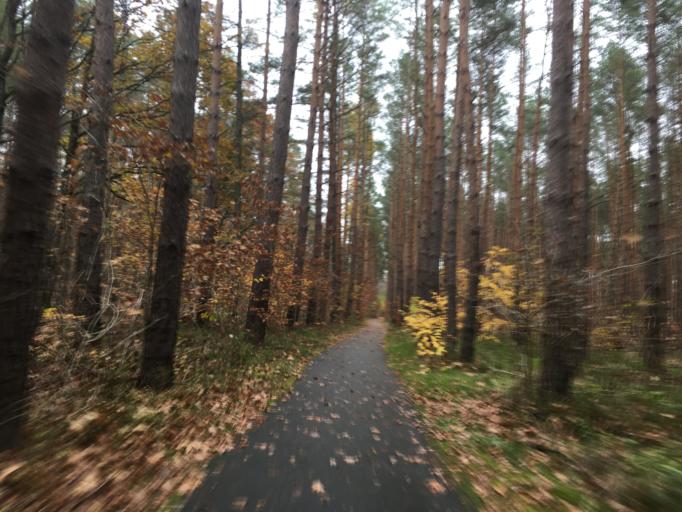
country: DE
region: Brandenburg
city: Mixdorf
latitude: 52.1532
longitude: 14.4350
